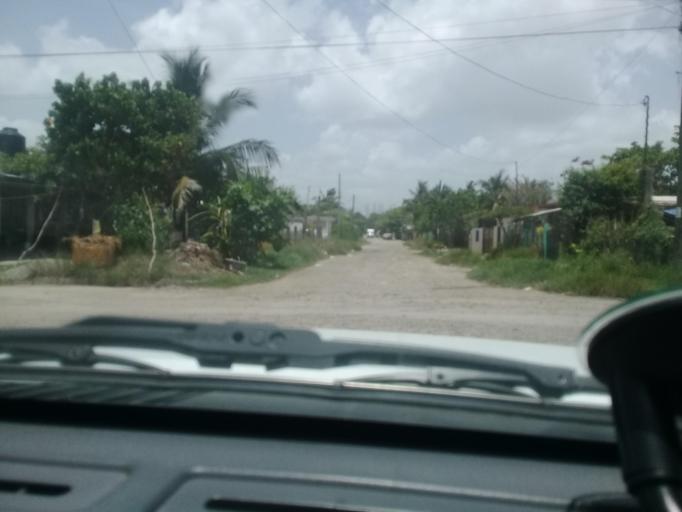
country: MX
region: Tamaulipas
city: Ciudad Madero
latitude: 22.2303
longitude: -97.8181
